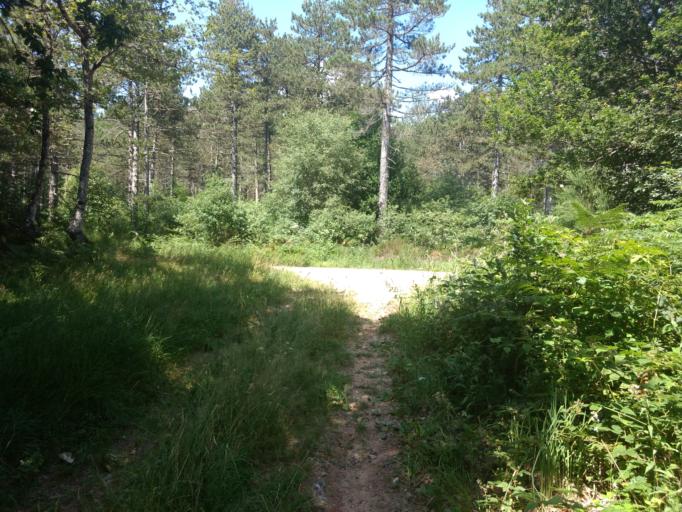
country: FR
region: Midi-Pyrenees
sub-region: Departement de l'Aveyron
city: Laissac
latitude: 44.3614
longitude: 2.7607
